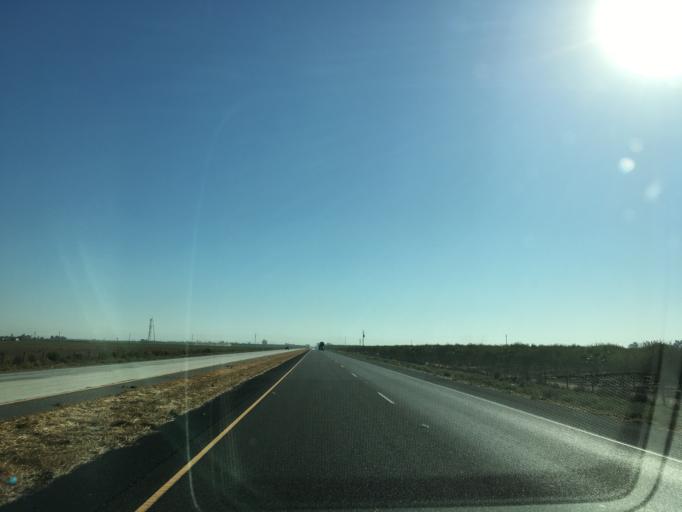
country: US
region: California
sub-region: Madera County
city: Chowchilla
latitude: 37.0834
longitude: -120.3390
